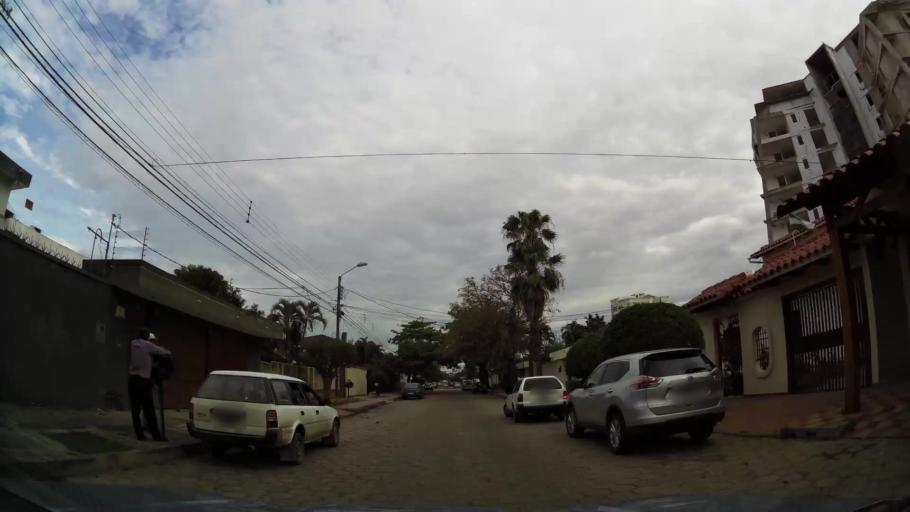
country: BO
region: Santa Cruz
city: Santa Cruz de la Sierra
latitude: -17.7904
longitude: -63.1746
